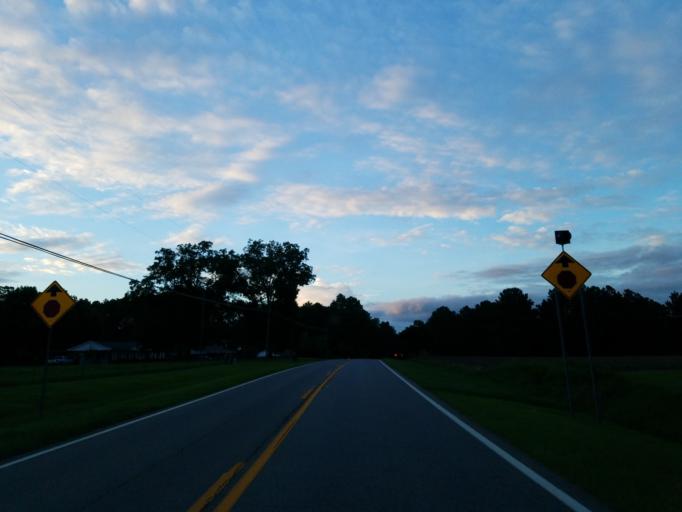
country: US
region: Georgia
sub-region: Tift County
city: Tifton
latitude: 31.5024
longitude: -83.5007
